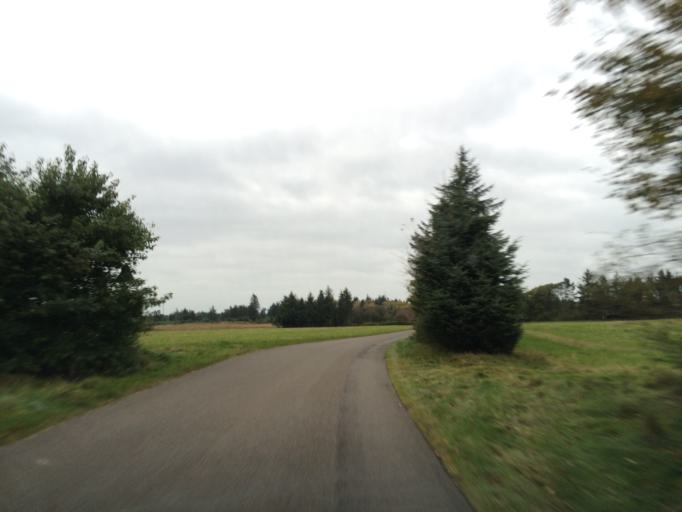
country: DK
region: Central Jutland
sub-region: Holstebro Kommune
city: Ulfborg
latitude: 56.2268
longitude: 8.4348
